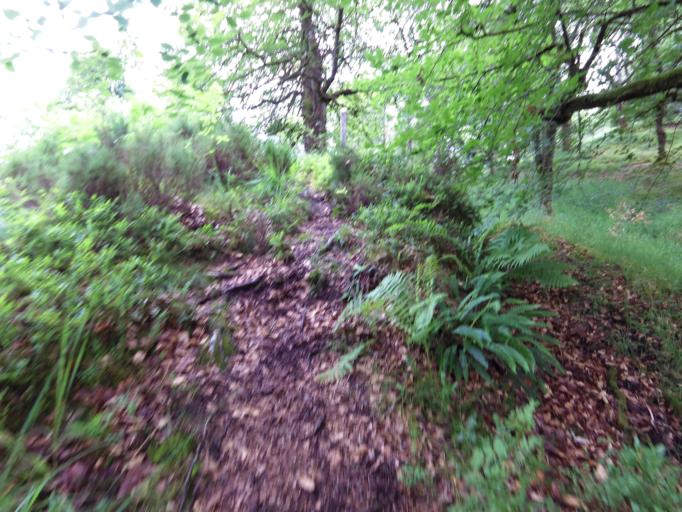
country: GB
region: Scotland
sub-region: Highland
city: Fort William
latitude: 56.8284
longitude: -5.1265
